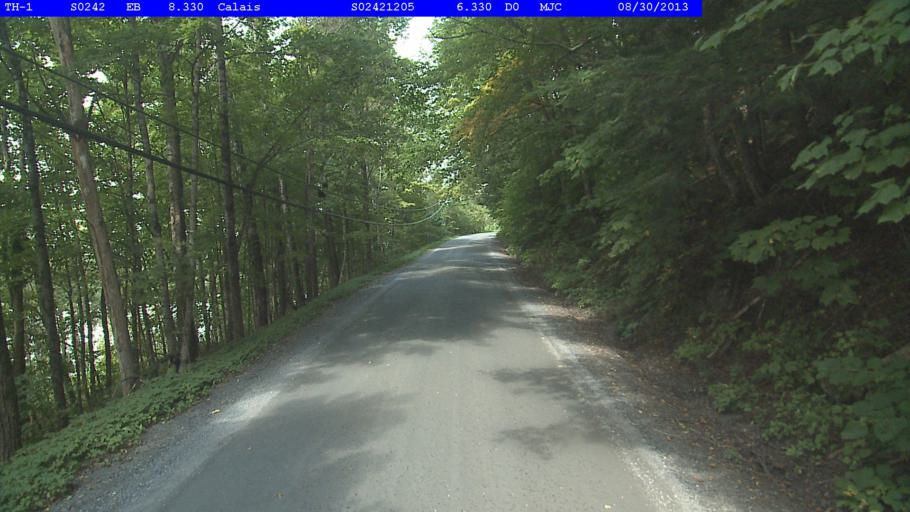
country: US
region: Vermont
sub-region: Caledonia County
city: Hardwick
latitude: 44.3918
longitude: -72.4431
